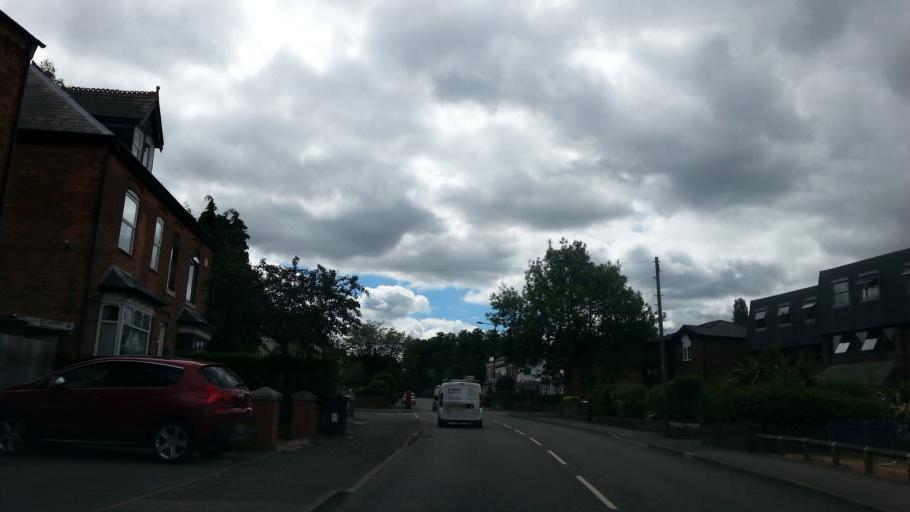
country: GB
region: England
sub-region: City and Borough of Birmingham
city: Sutton Coldfield
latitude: 52.5449
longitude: -1.8401
